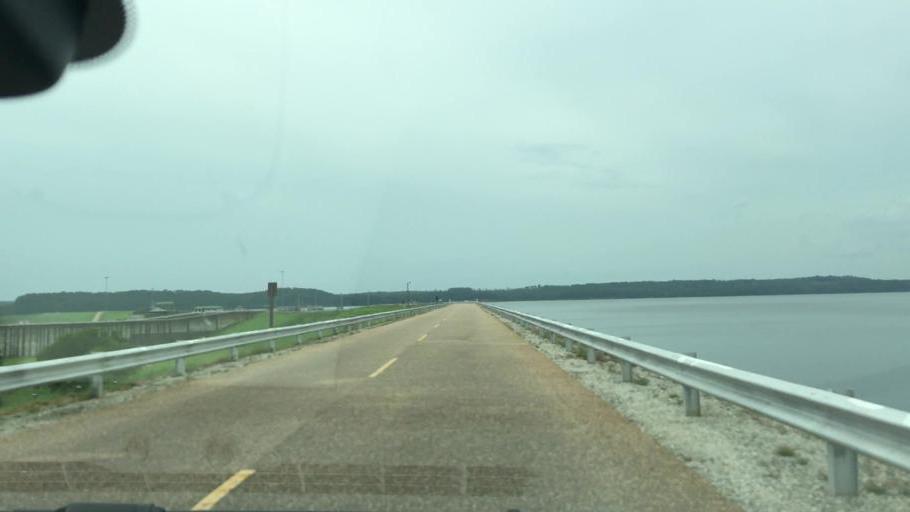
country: US
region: Georgia
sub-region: Clay County
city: Fort Gaines
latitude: 31.6289
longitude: -85.0578
